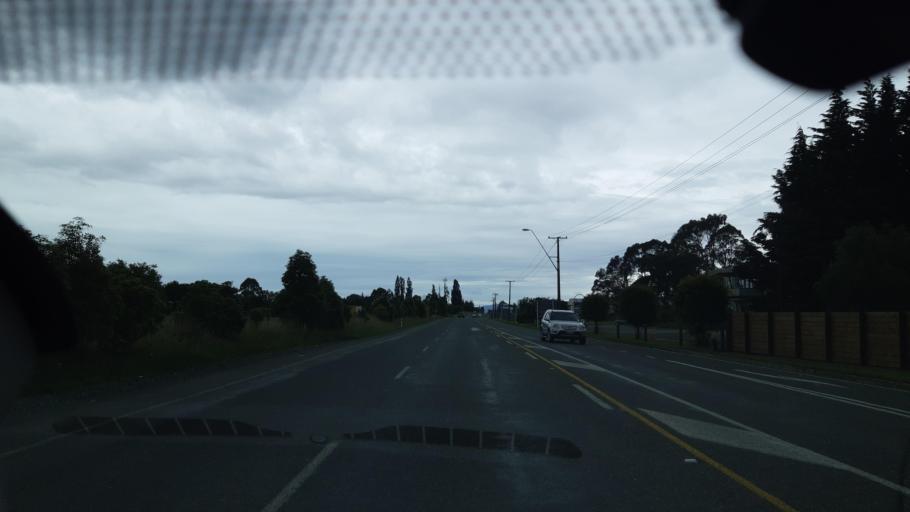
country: NZ
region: Tasman
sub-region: Tasman District
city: Brightwater
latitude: -41.3790
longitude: 173.1145
